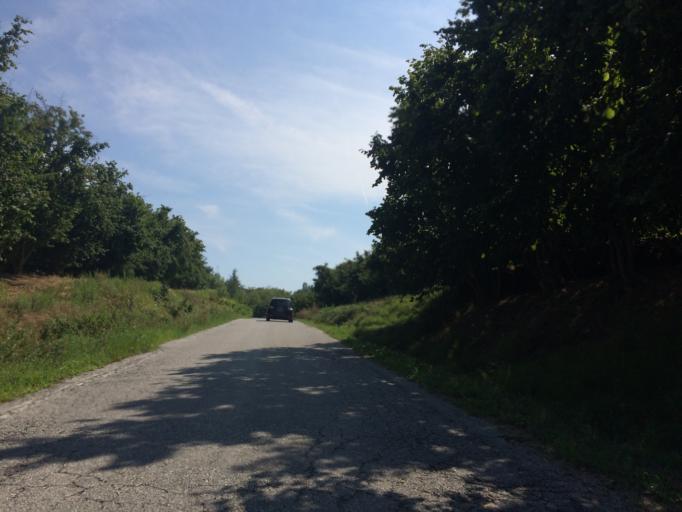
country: IT
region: Piedmont
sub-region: Provincia di Cuneo
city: Cravanzana
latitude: 44.5832
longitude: 8.1318
